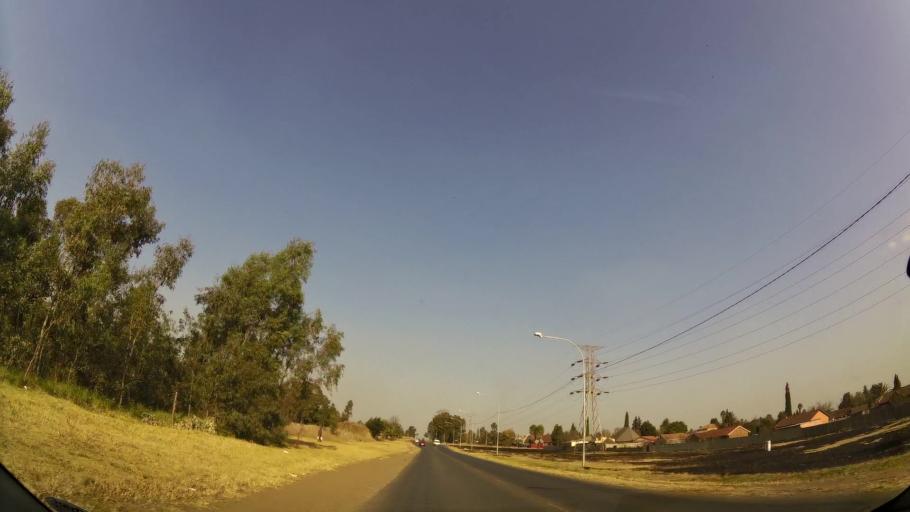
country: ZA
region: Gauteng
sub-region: Ekurhuleni Metropolitan Municipality
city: Benoni
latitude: -26.1134
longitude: 28.3732
